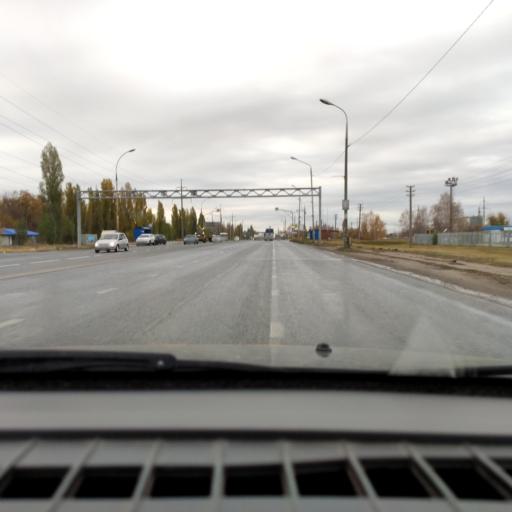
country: RU
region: Samara
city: Tol'yatti
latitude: 53.5643
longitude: 49.2902
